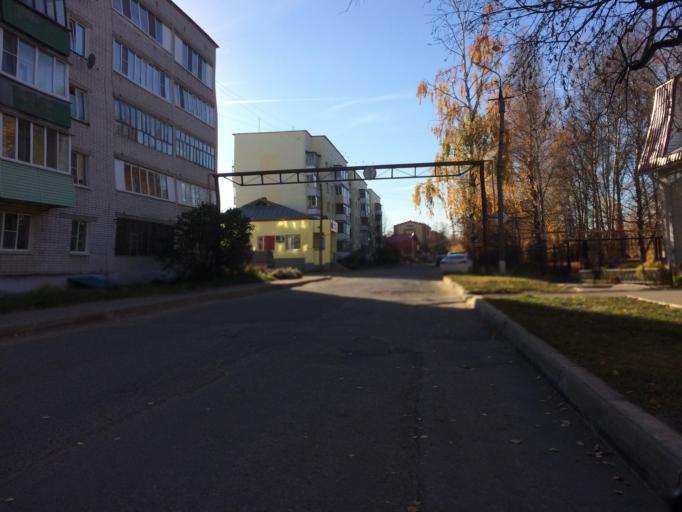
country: RU
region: Mariy-El
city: Medvedevo
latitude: 56.6329
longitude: 47.8085
